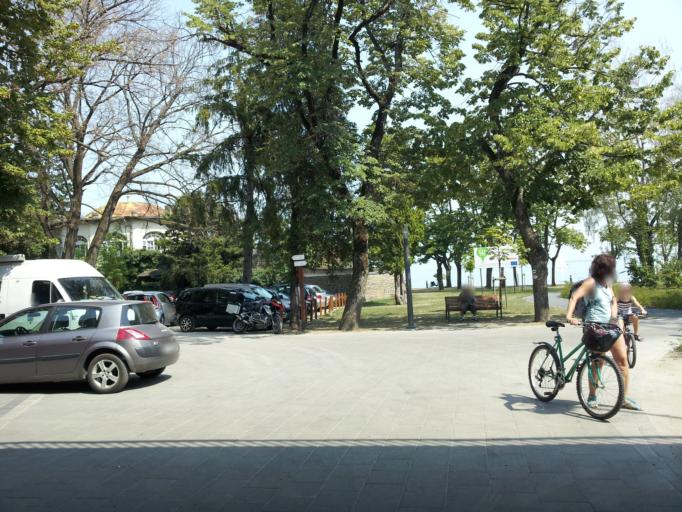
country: HU
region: Veszprem
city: Tihany
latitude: 46.9162
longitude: 17.8919
